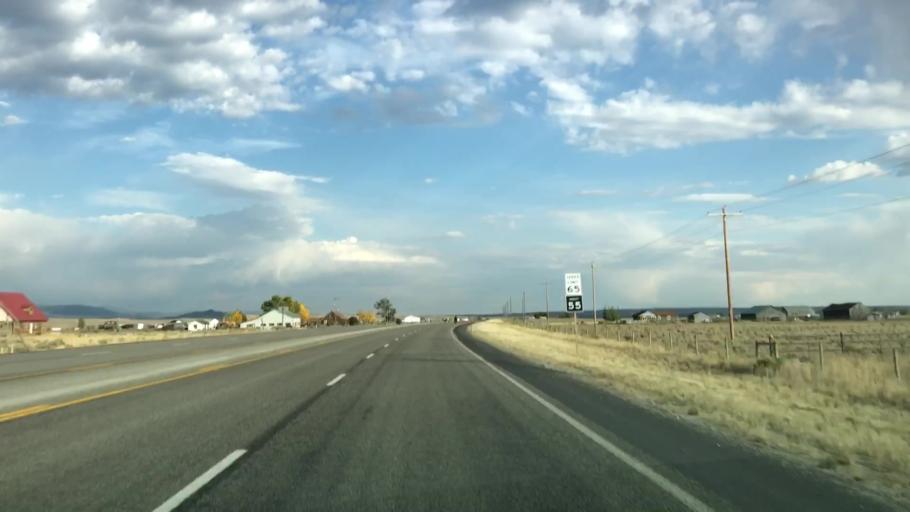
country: US
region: Wyoming
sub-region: Sublette County
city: Pinedale
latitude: 42.7840
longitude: -109.7691
